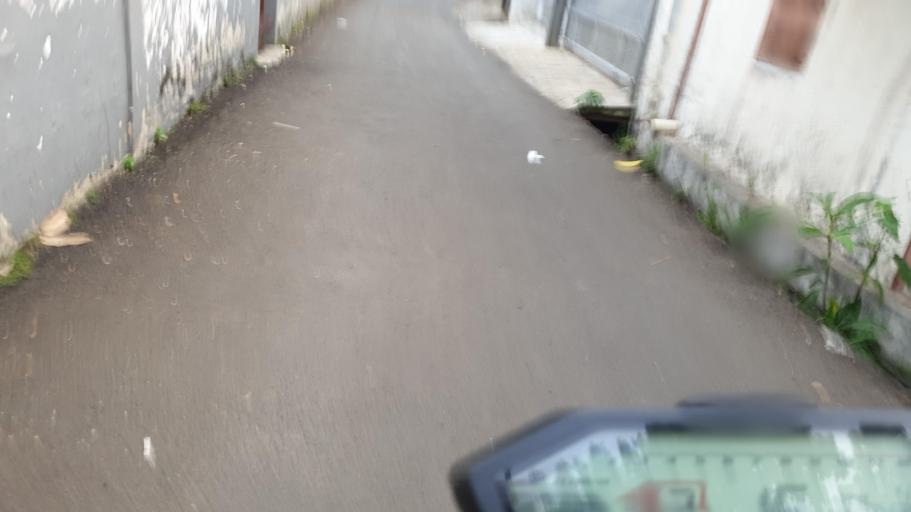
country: ID
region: West Java
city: Depok
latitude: -6.3647
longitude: 106.8384
